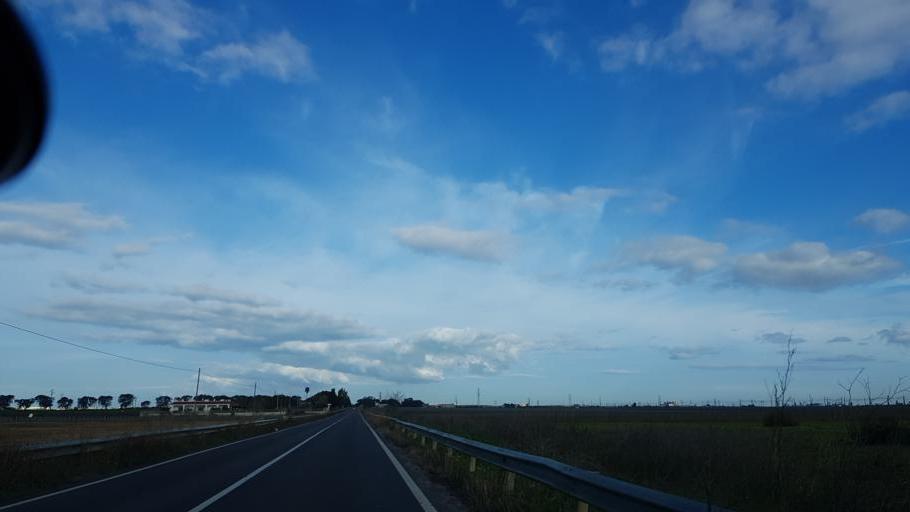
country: IT
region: Apulia
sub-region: Provincia di Brindisi
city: Tuturano
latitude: 40.5743
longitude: 17.9670
